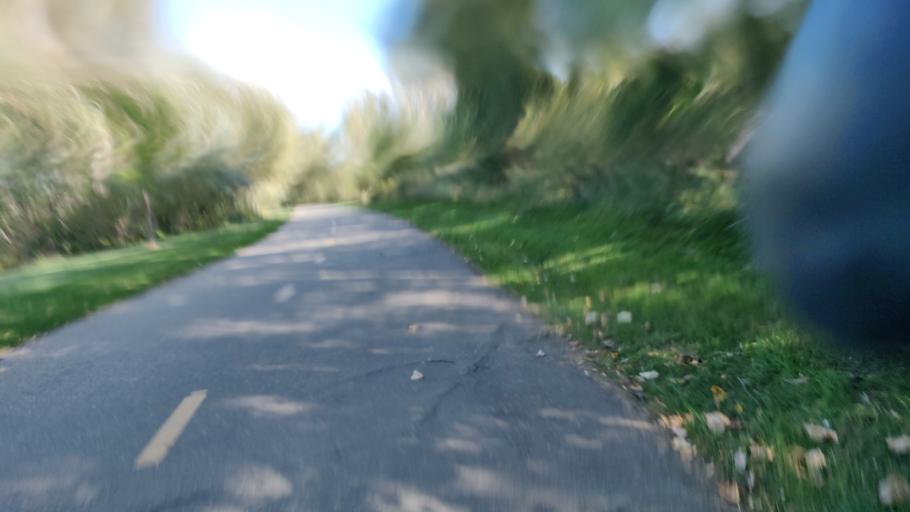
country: US
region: Idaho
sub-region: Ada County
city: Boise
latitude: 43.5755
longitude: -116.1500
